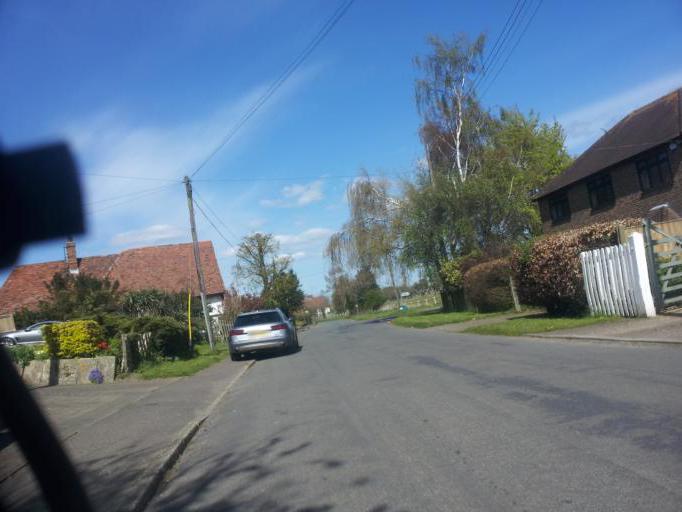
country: GB
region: England
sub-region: Kent
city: Newington
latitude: 51.3264
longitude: 0.6412
